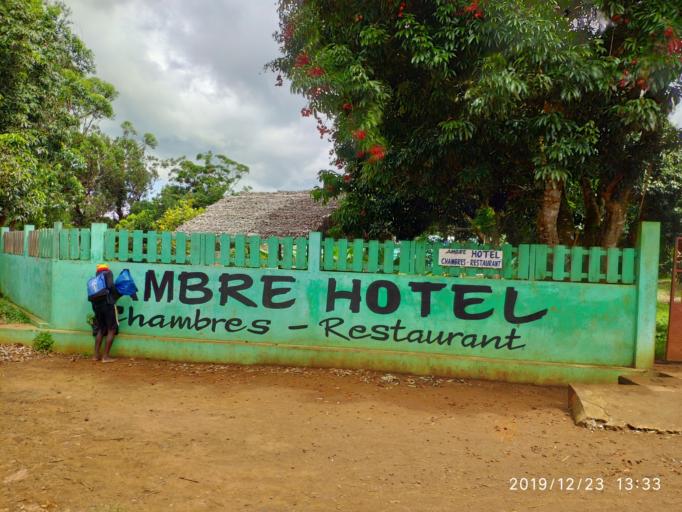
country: MG
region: Diana
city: Sadjoavato
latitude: -12.5028
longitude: 49.2010
